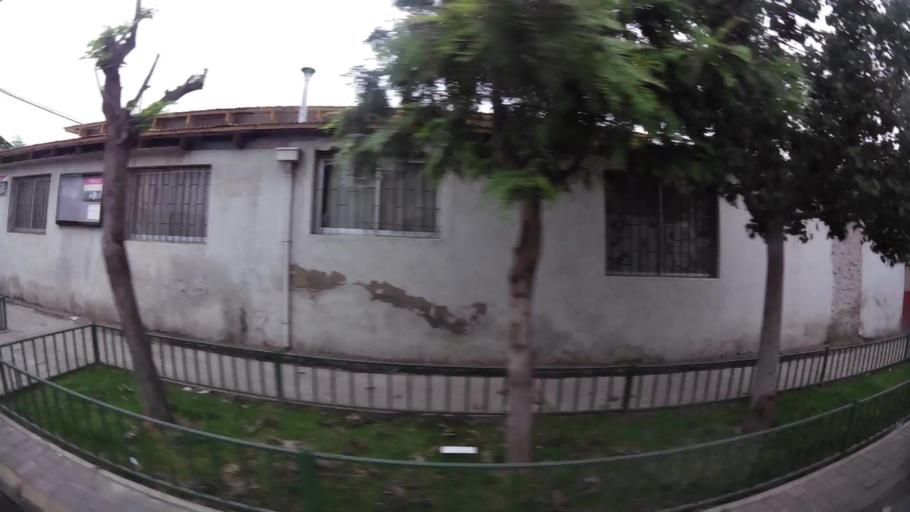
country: CL
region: Santiago Metropolitan
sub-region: Provincia de Santiago
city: Santiago
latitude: -33.4979
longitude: -70.6373
